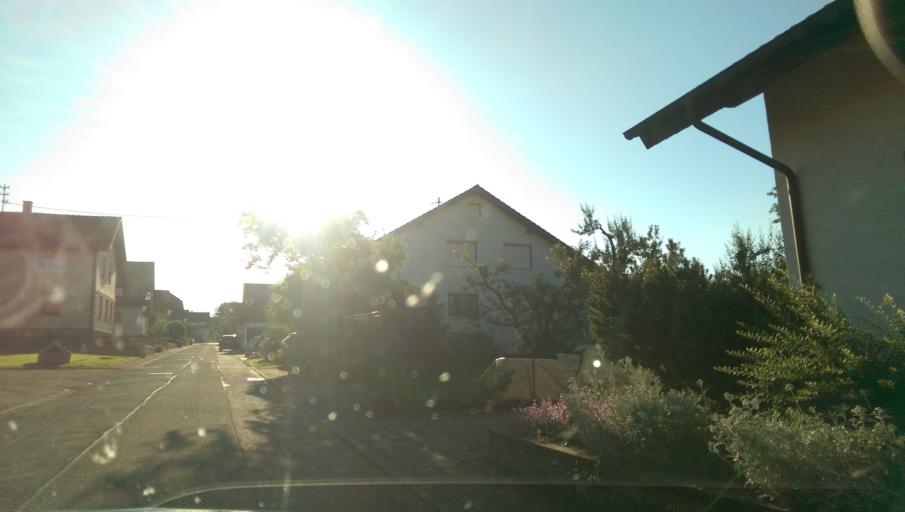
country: DE
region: Baden-Wuerttemberg
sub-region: Karlsruhe Region
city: Dobel
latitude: 48.8444
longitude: 8.4969
